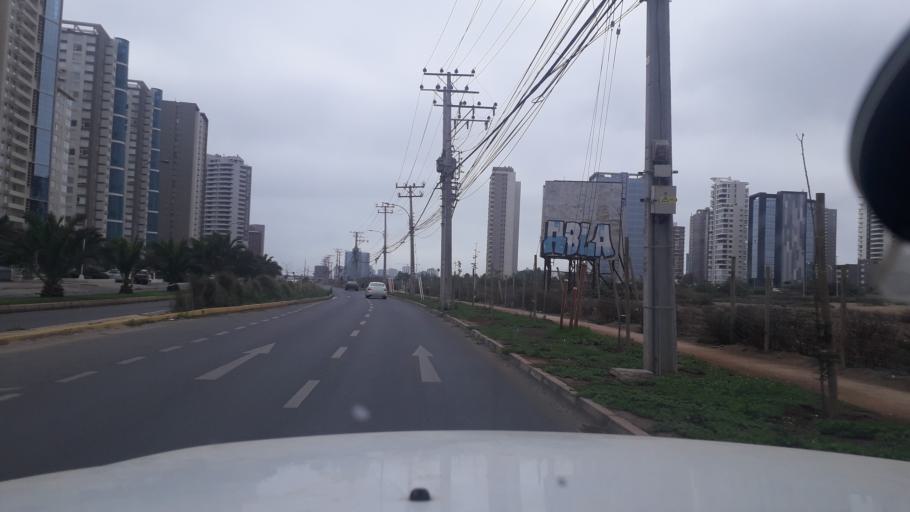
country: CL
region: Valparaiso
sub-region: Provincia de Valparaiso
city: Vina del Mar
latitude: -32.9533
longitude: -71.5439
